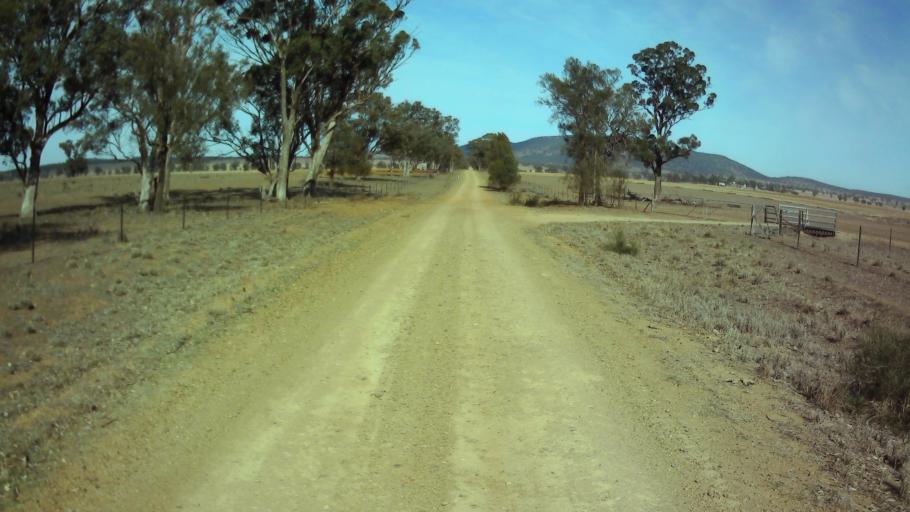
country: AU
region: New South Wales
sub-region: Weddin
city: Grenfell
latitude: -33.7524
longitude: 148.0082
